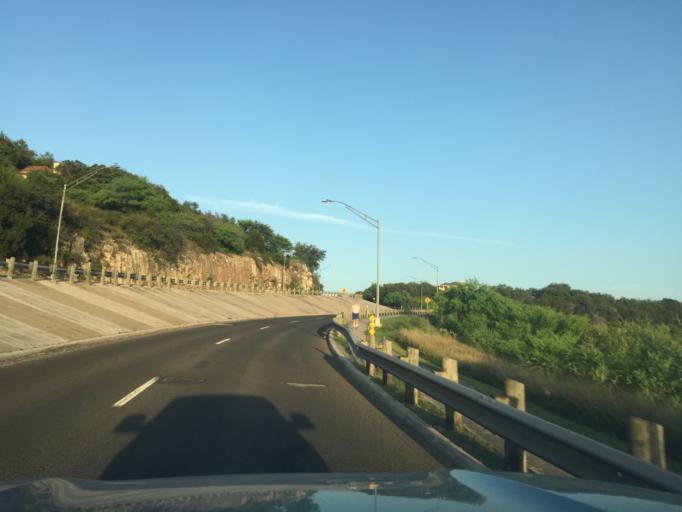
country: US
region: Texas
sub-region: Bexar County
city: Hollywood Park
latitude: 29.6401
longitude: -98.4658
